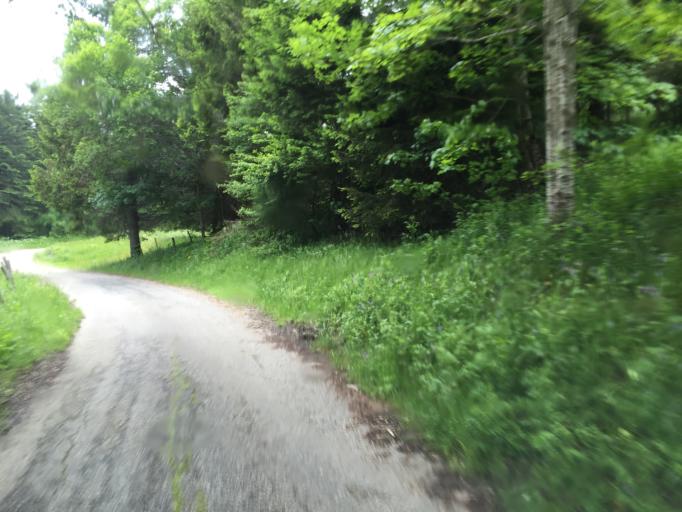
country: FR
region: Rhone-Alpes
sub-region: Departement de la Savoie
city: Cruet
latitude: 45.6236
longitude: 6.1236
